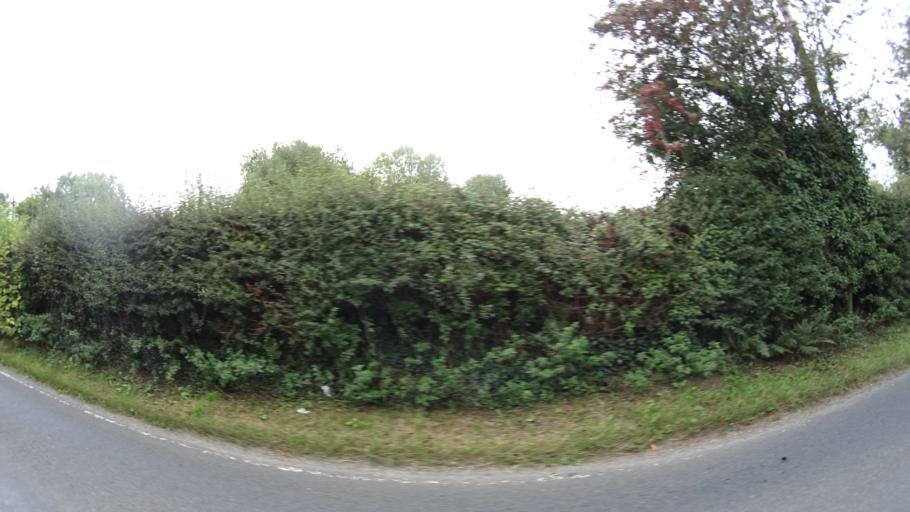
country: GB
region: England
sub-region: Dorset
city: Shaftesbury
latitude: 51.0102
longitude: -2.2023
